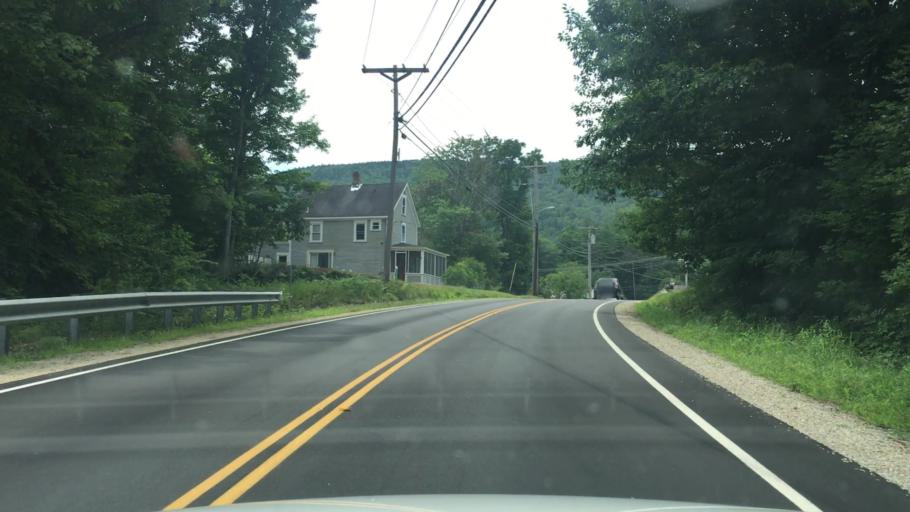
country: US
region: New Hampshire
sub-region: Grafton County
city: Rumney
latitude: 43.7969
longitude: -71.8163
